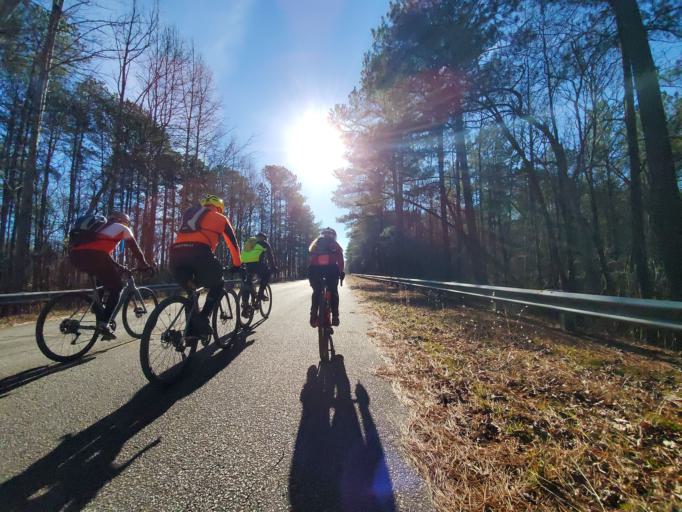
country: US
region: Georgia
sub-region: Fulton County
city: Chattahoochee Hills
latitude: 33.5693
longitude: -84.7891
